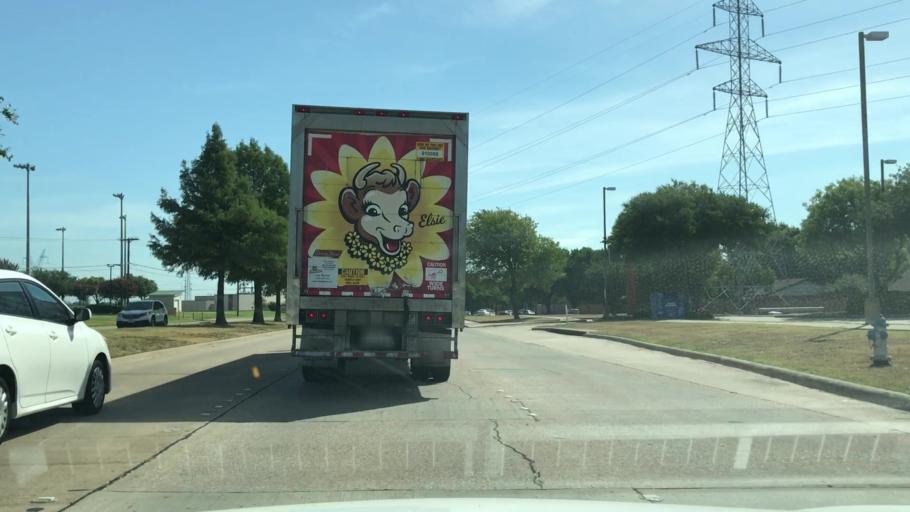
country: US
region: Texas
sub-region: Collin County
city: Plano
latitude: 33.0570
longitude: -96.7063
